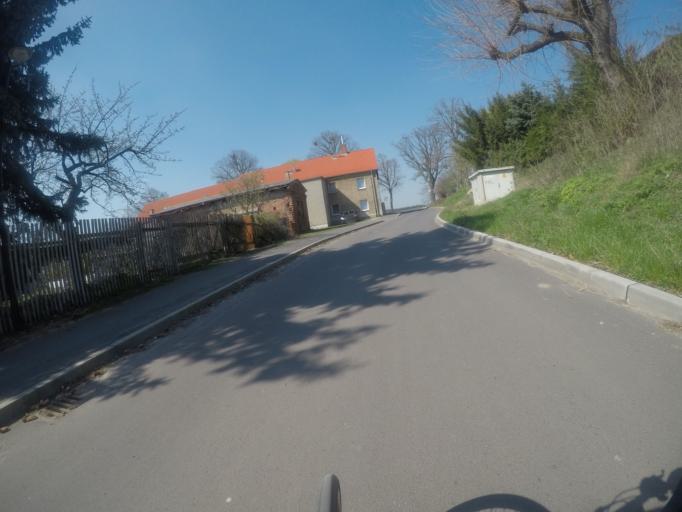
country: DE
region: Brandenburg
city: Brieselang
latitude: 52.6530
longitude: 13.0103
